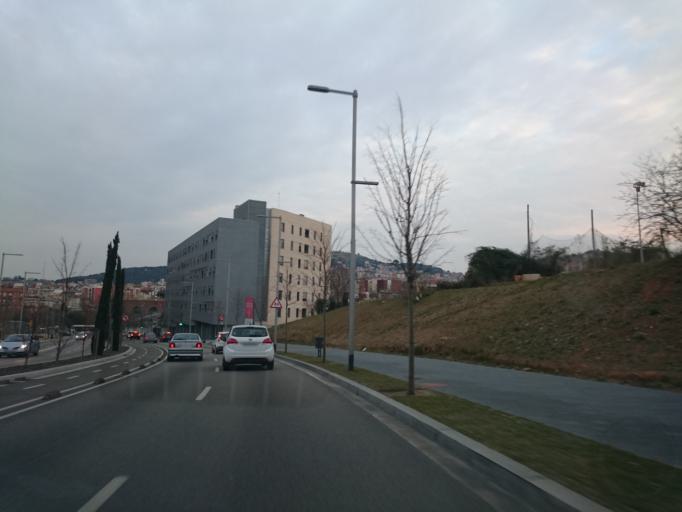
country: ES
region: Catalonia
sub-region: Provincia de Barcelona
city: Horta-Guinardo
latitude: 41.4314
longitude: 2.1540
